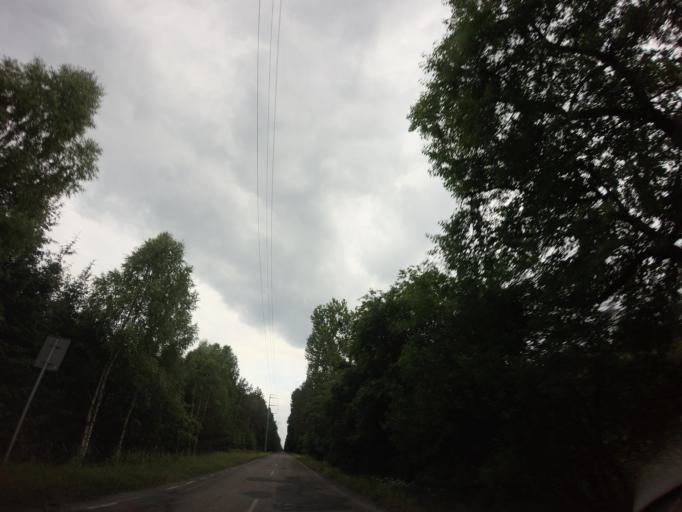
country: PL
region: West Pomeranian Voivodeship
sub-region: Powiat drawski
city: Czaplinek
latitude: 53.4591
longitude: 16.2176
